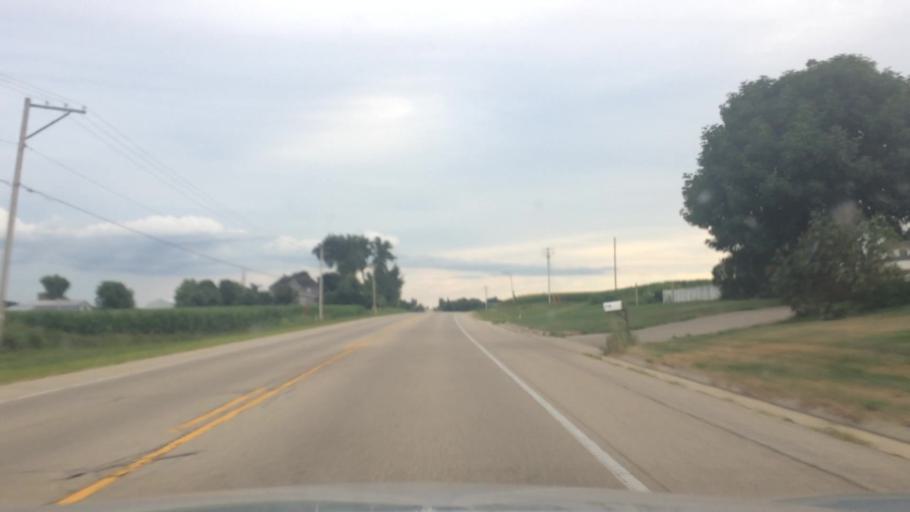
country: US
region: Wisconsin
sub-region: Columbia County
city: Lodi
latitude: 43.2845
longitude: -89.5214
